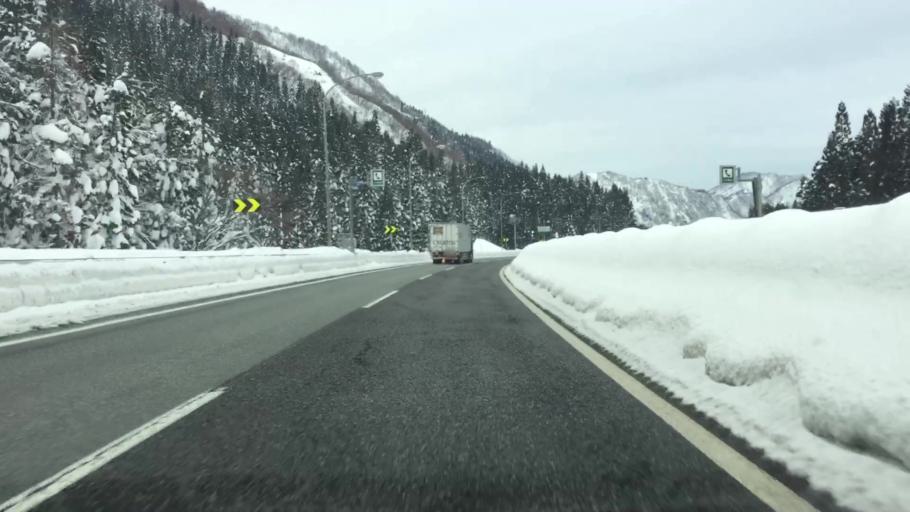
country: JP
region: Niigata
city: Shiozawa
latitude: 36.8866
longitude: 138.8498
